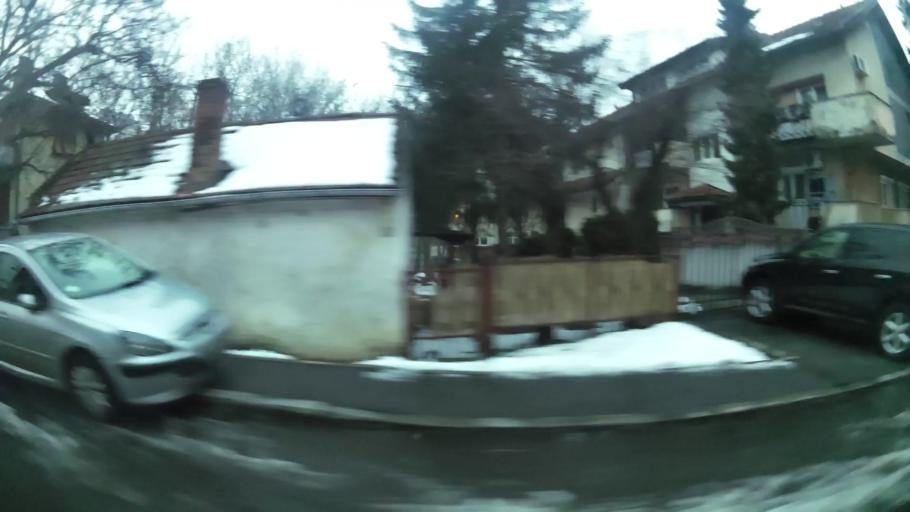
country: RS
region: Central Serbia
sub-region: Belgrade
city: Vozdovac
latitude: 44.7741
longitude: 20.4878
